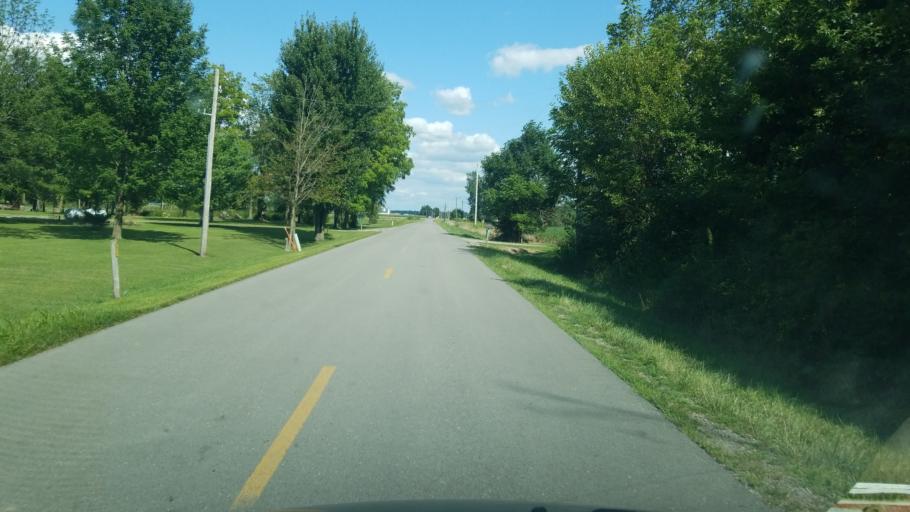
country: US
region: Ohio
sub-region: Logan County
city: Lakeview
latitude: 40.5135
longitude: -83.9409
